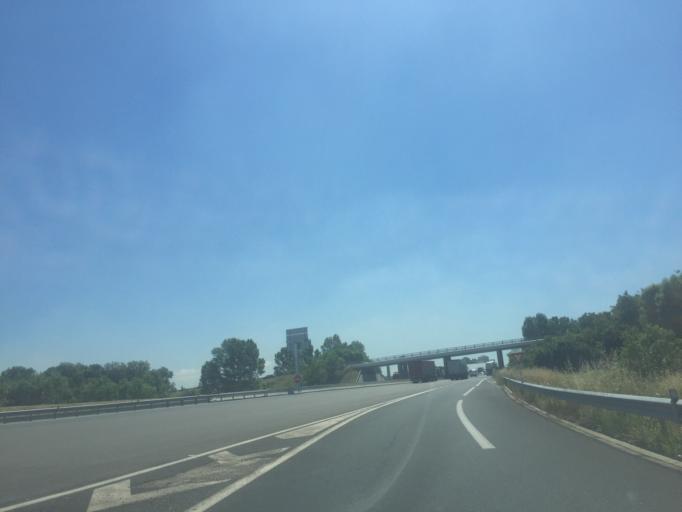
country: FR
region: Rhone-Alpes
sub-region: Departement de l'Ain
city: Thil
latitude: 45.8261
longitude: 5.0333
